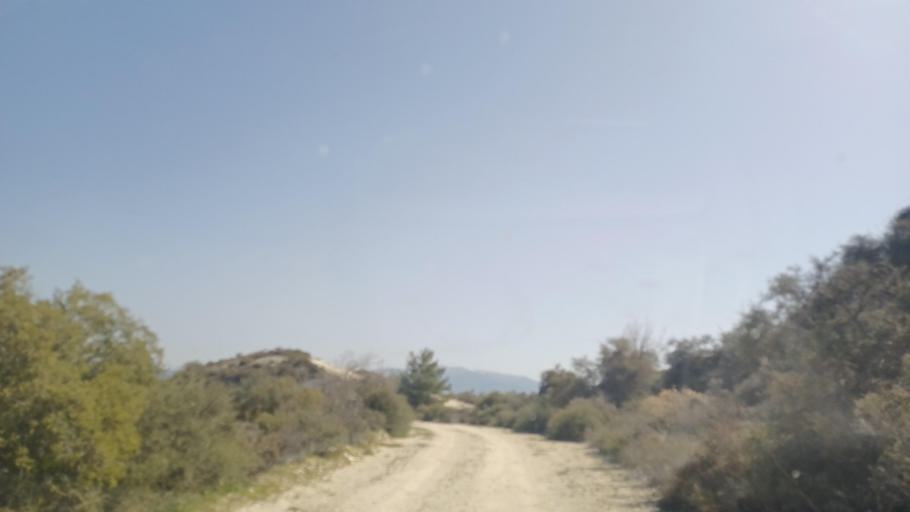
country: CY
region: Limassol
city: Pachna
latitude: 34.8732
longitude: 32.7047
